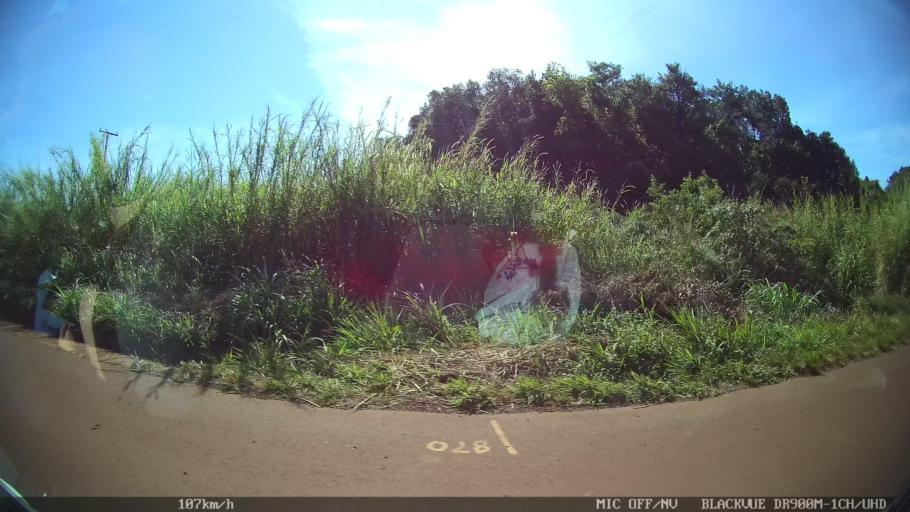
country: BR
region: Sao Paulo
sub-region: Ipua
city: Ipua
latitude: -20.4922
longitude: -48.0013
